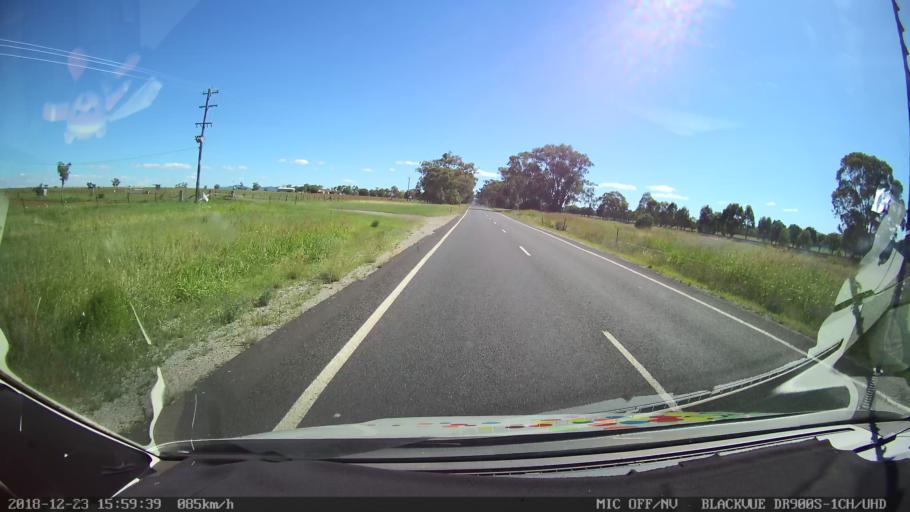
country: AU
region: New South Wales
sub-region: Tamworth Municipality
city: Phillip
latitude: -31.2021
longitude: 150.8315
